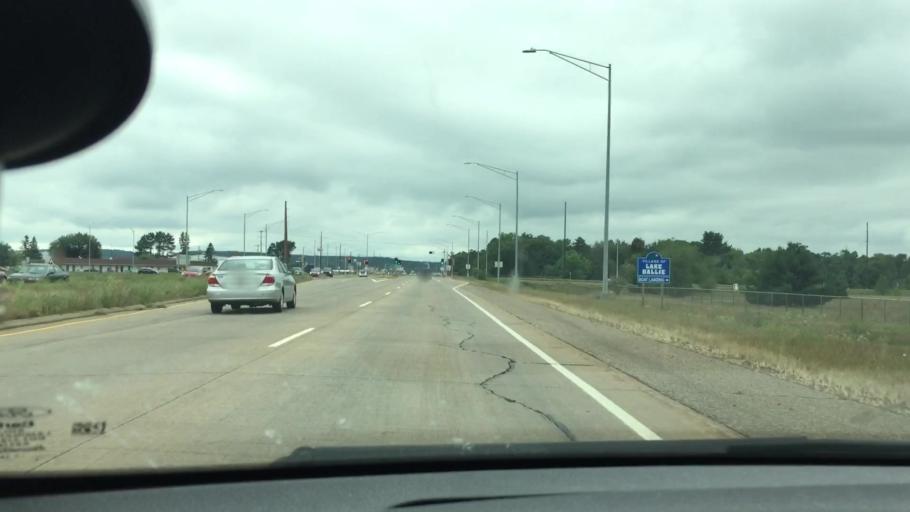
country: US
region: Wisconsin
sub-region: Chippewa County
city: Lake Hallie
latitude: 44.8882
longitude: -91.4209
